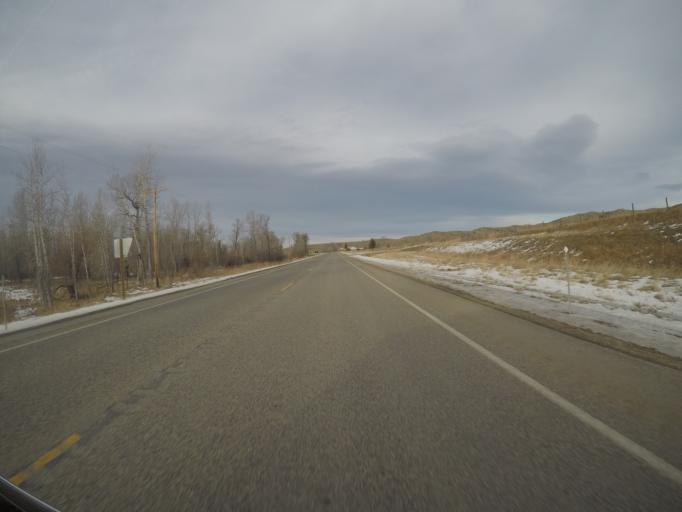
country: US
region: Montana
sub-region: Stillwater County
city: Absarokee
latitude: 45.4625
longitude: -109.4486
